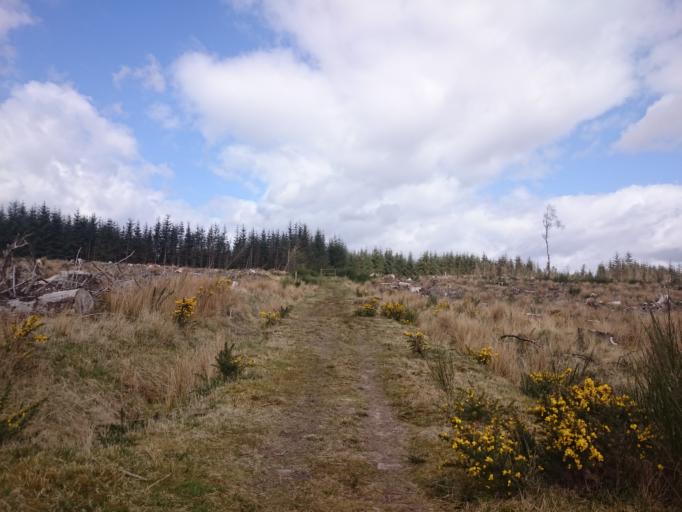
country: GB
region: Scotland
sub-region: Stirling
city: Killearn
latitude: 56.0782
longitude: -4.4318
